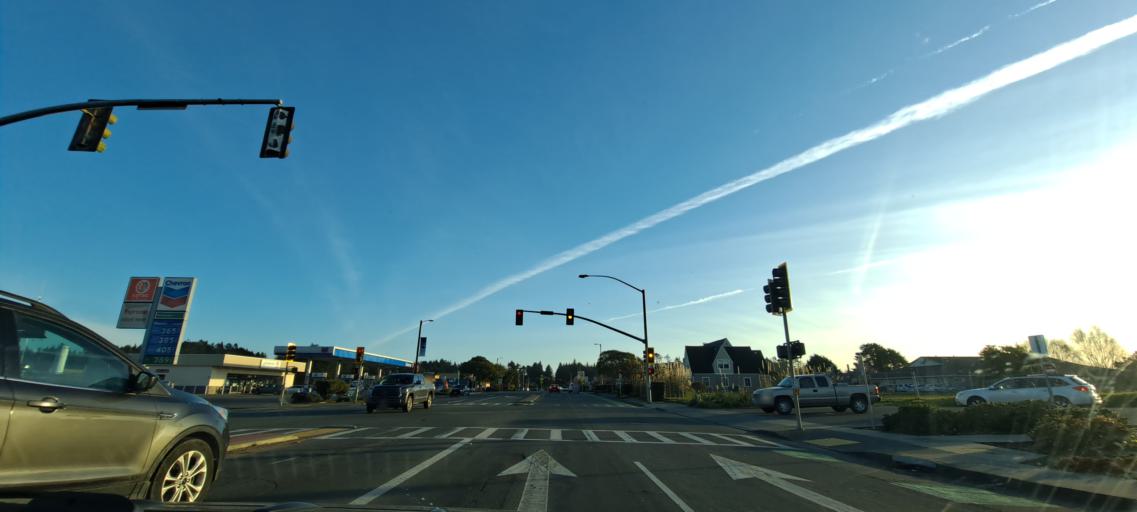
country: US
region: California
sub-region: Humboldt County
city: McKinleyville
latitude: 40.9363
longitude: -124.1010
